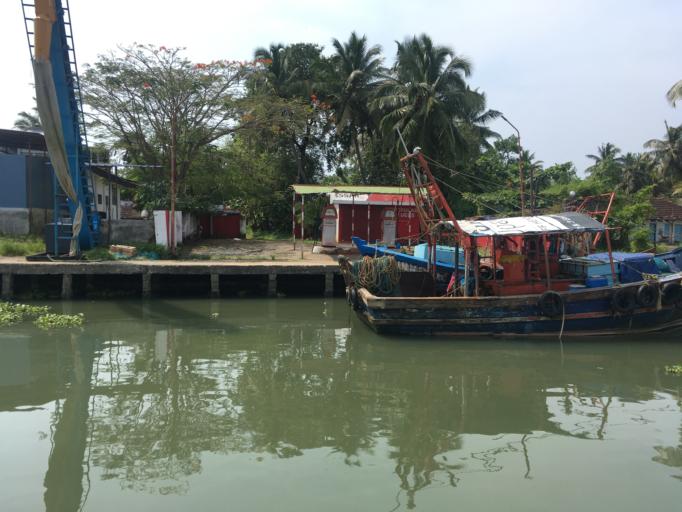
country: IN
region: Kerala
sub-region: Ernakulam
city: Cochin
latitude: 9.9804
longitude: 76.2418
